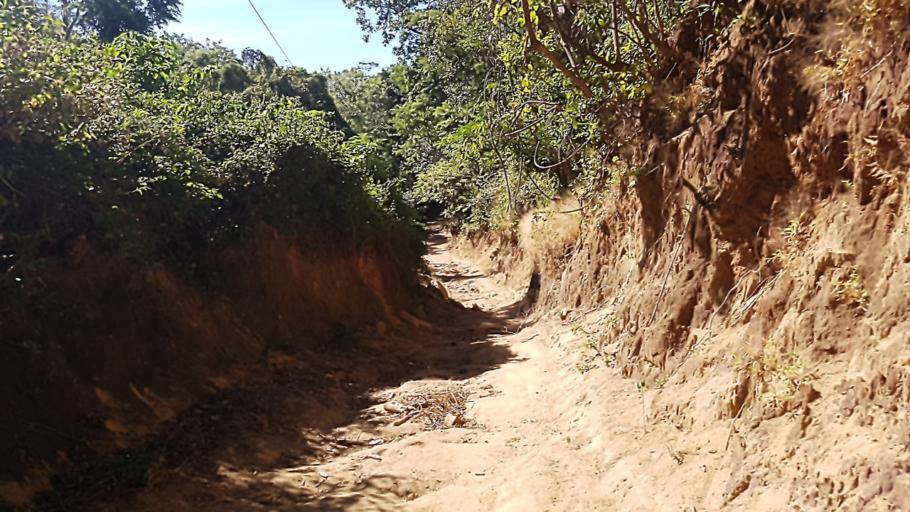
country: NI
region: Carazo
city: Santa Teresa
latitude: 11.6620
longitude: -86.1748
